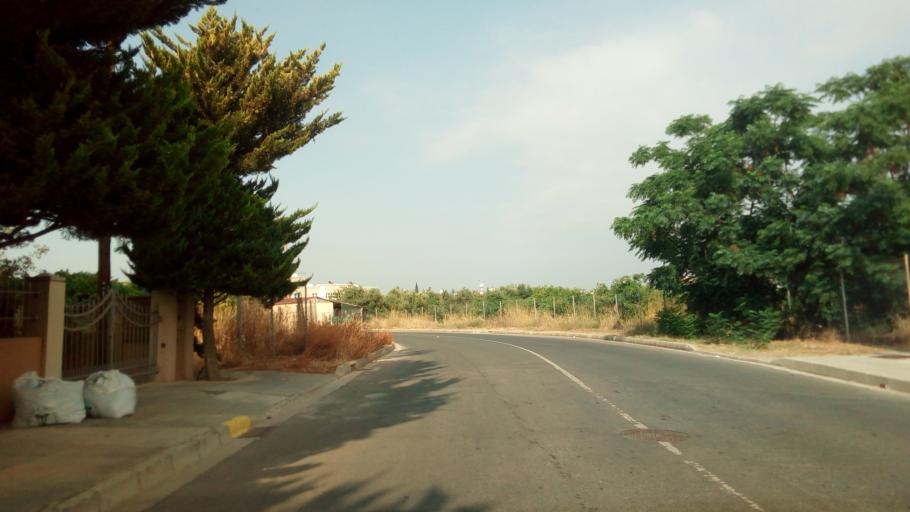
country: CY
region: Limassol
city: Pano Polemidia
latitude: 34.6915
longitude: 33.0065
